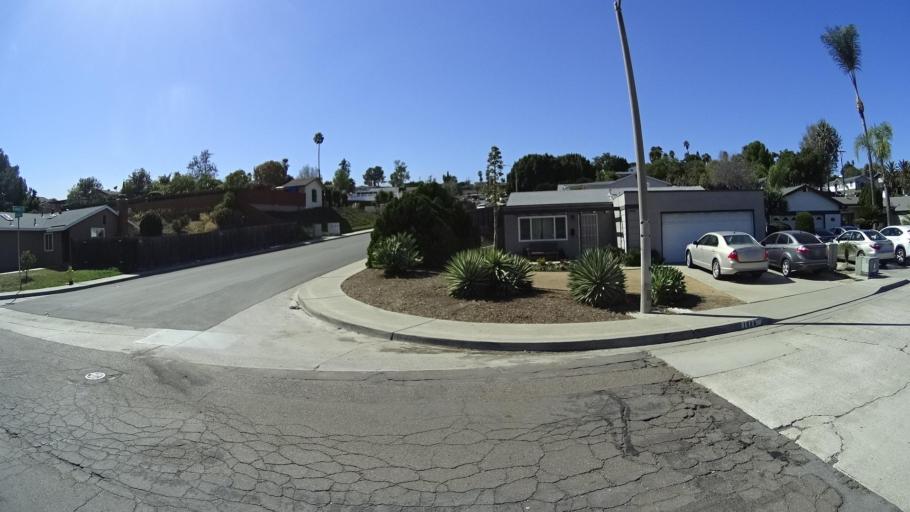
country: US
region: California
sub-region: San Diego County
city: La Presa
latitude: 32.7140
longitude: -117.0202
